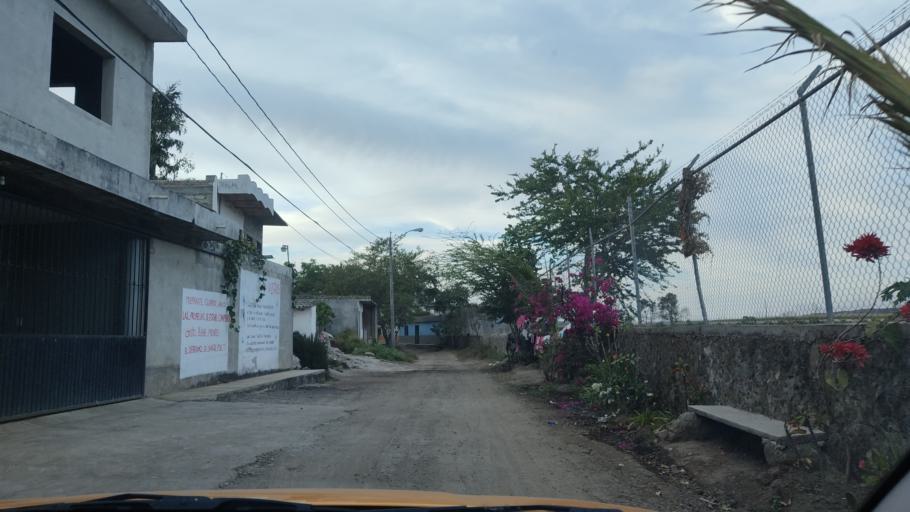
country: MX
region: Nayarit
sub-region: Tepic
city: La Corregidora
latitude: 21.4572
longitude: -104.8202
